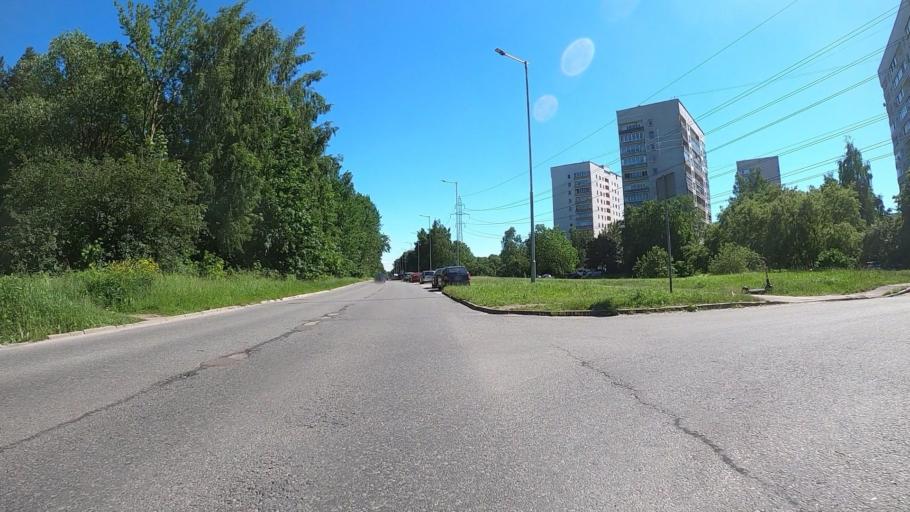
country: LV
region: Riga
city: Jaunciems
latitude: 56.9612
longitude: 24.2005
